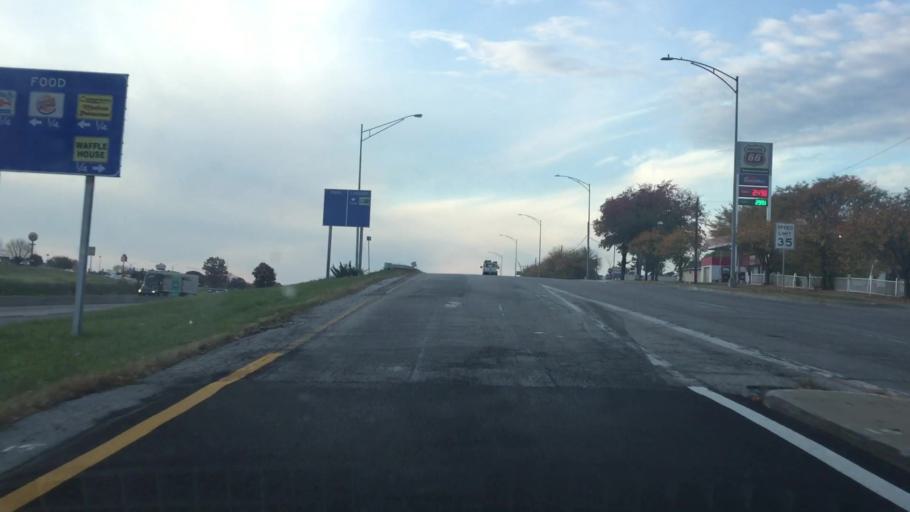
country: US
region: Missouri
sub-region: Jackson County
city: Grandview
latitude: 38.8923
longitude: -94.5253
